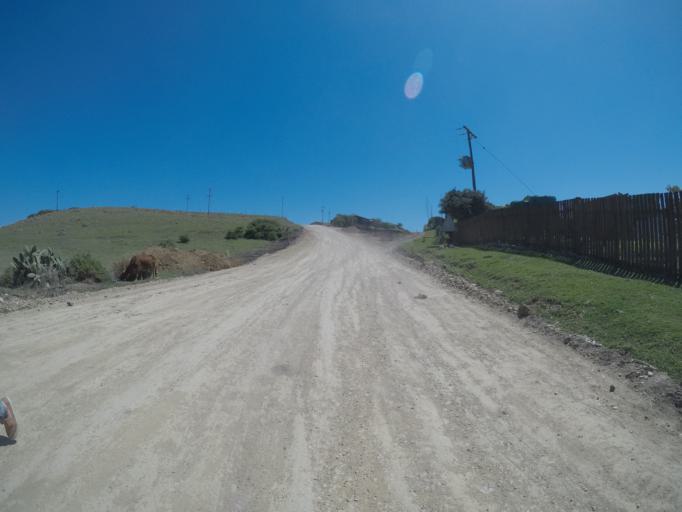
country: ZA
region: Eastern Cape
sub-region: OR Tambo District Municipality
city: Libode
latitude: -32.0353
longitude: 29.1106
